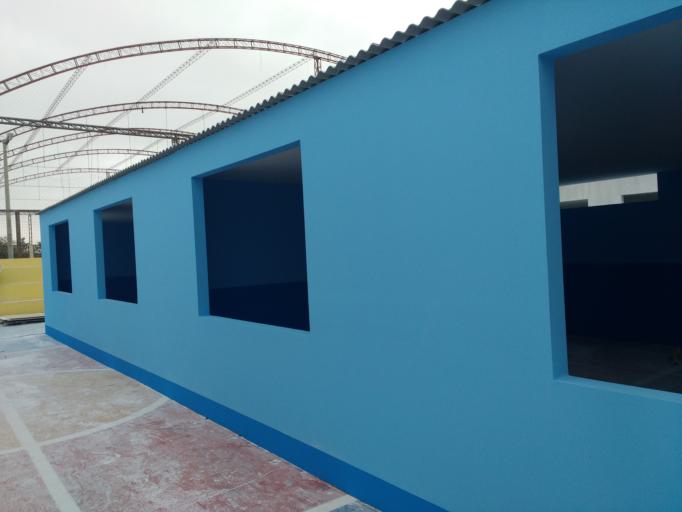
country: PE
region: Ica
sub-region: Provincia de Pisco
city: Villa Tupac Amaru
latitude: -13.8312
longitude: -76.1383
